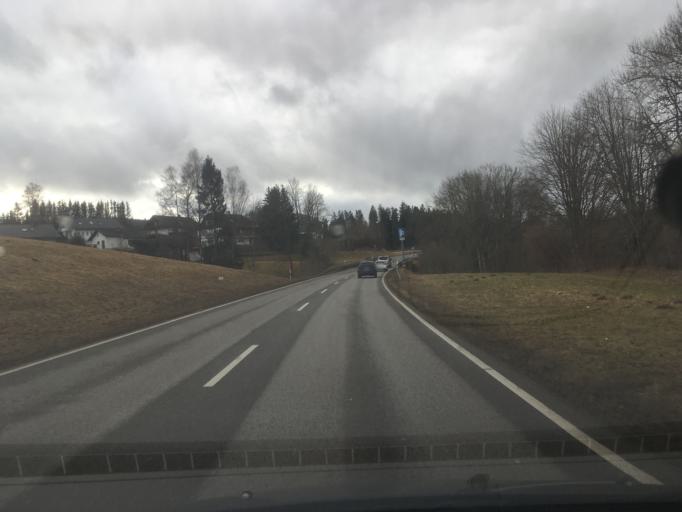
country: DE
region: Baden-Wuerttemberg
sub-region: Freiburg Region
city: Hausern
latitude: 47.7516
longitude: 8.1654
